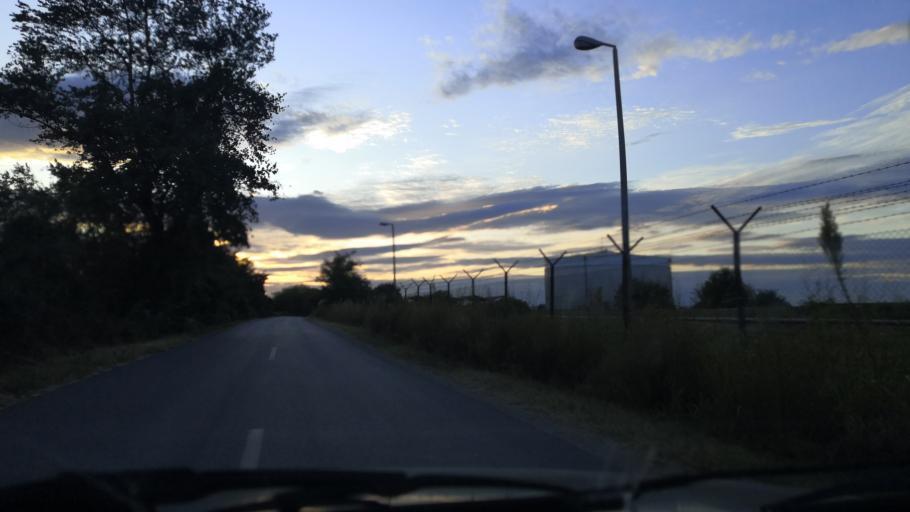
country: RO
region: Mehedinti
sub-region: Comuna Gruia
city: Izvoarele
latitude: 44.2866
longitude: 22.6285
